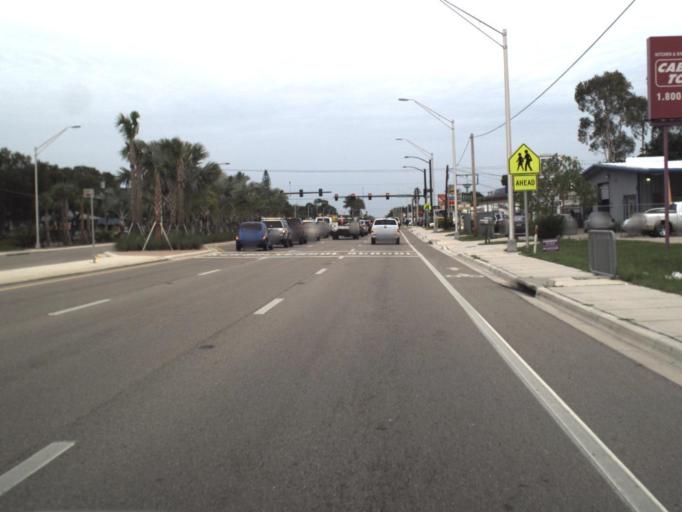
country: US
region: Florida
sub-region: Sarasota County
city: North Sarasota
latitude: 27.3580
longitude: -82.5304
